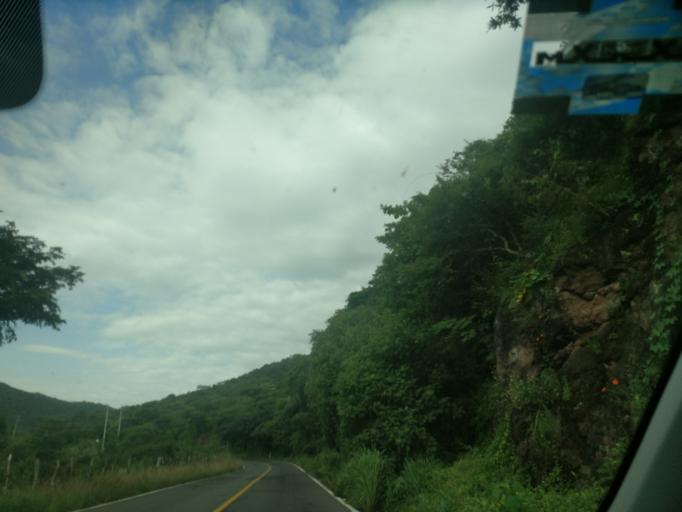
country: MX
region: Jalisco
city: Ameca
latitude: 20.5283
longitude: -104.2169
